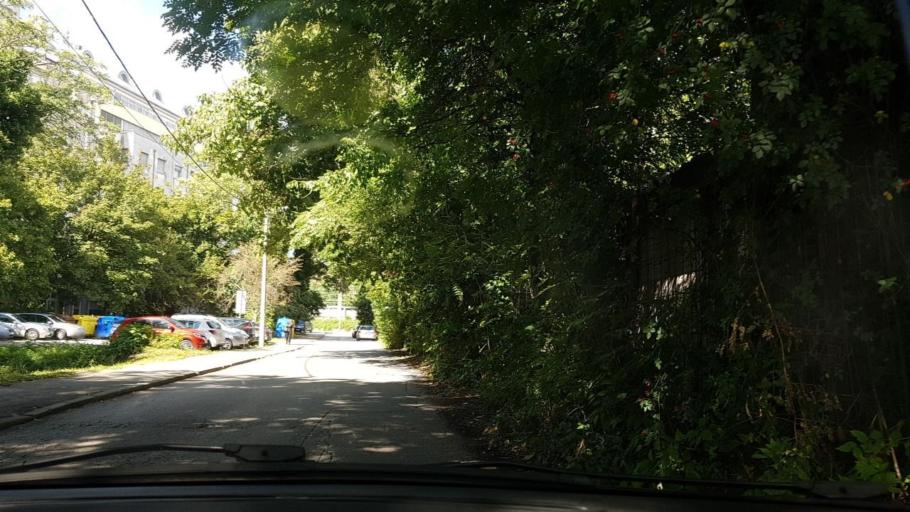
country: HR
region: Grad Zagreb
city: Zagreb - Centar
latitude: 45.8021
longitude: 15.9702
